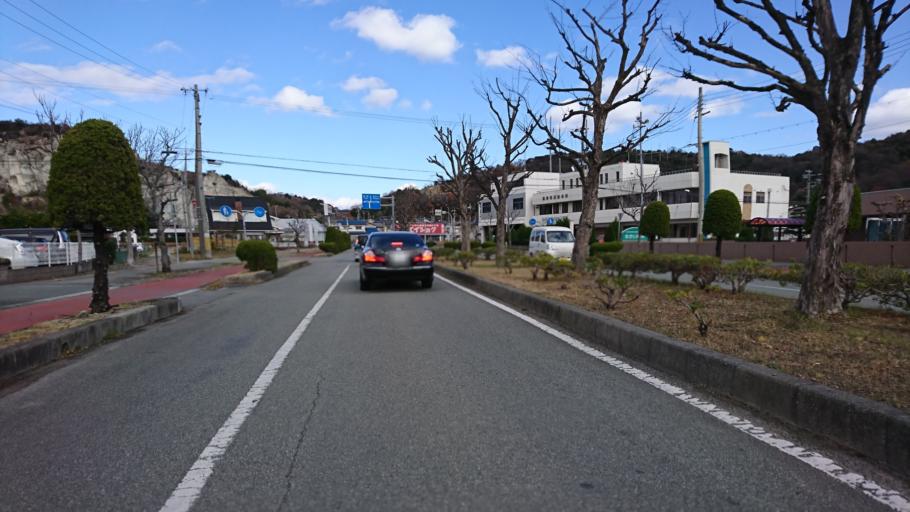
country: JP
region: Hyogo
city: Kakogawacho-honmachi
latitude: 34.7770
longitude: 134.7903
